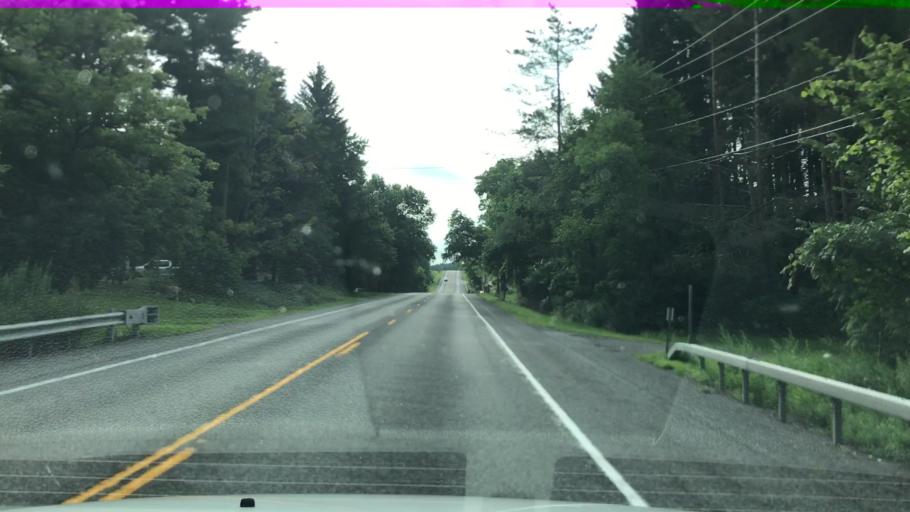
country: US
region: New York
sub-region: Erie County
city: Alden
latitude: 42.8391
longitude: -78.4581
